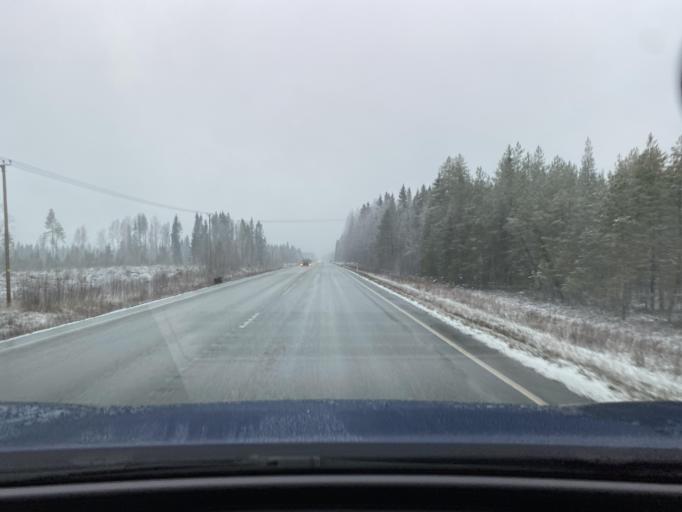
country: FI
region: Northern Ostrobothnia
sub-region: Oulu
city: Kiiminki
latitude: 65.1451
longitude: 25.8913
